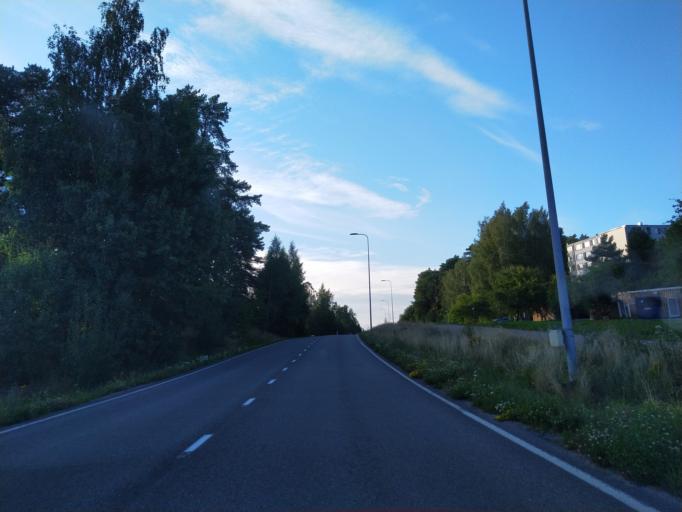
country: FI
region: Varsinais-Suomi
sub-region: Turku
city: Kaarina
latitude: 60.4093
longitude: 22.3151
